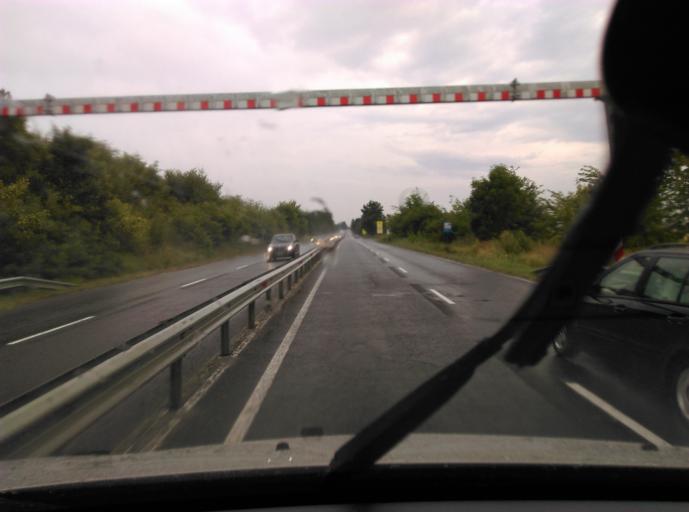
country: BG
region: Burgas
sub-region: Obshtina Burgas
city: Burgas
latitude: 42.4401
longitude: 27.4785
